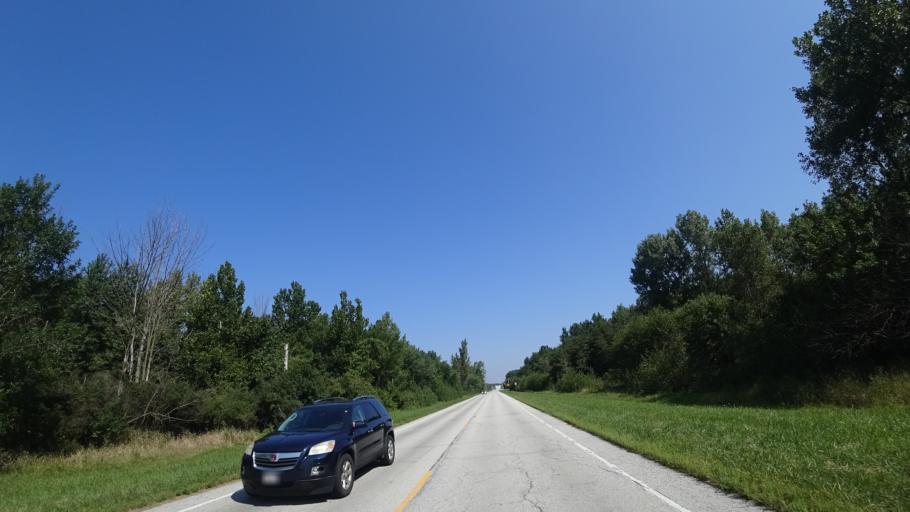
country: US
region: Illinois
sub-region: Cook County
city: Country Club Hills
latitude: 41.5535
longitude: -87.7523
